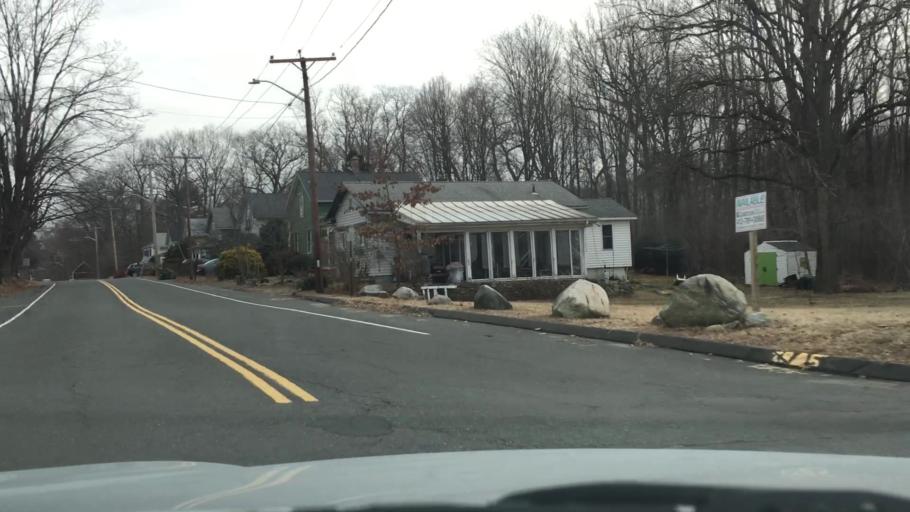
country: US
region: Massachusetts
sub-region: Hampshire County
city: Northampton
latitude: 42.3206
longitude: -72.6642
